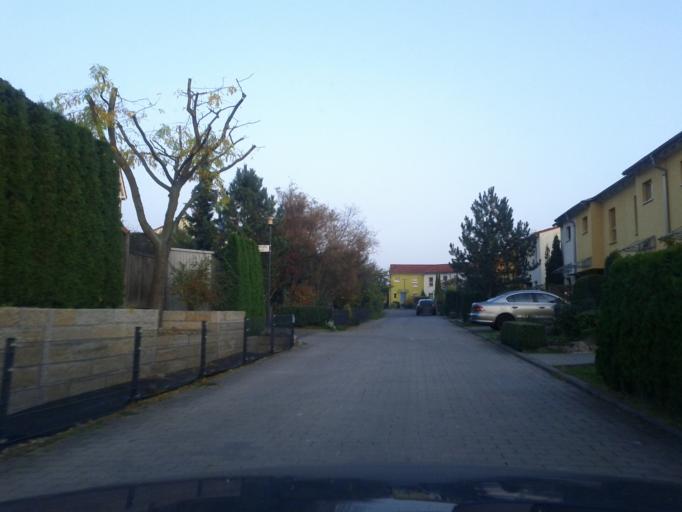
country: DE
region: Berlin
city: Mahlsdorf
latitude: 52.4983
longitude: 13.6227
